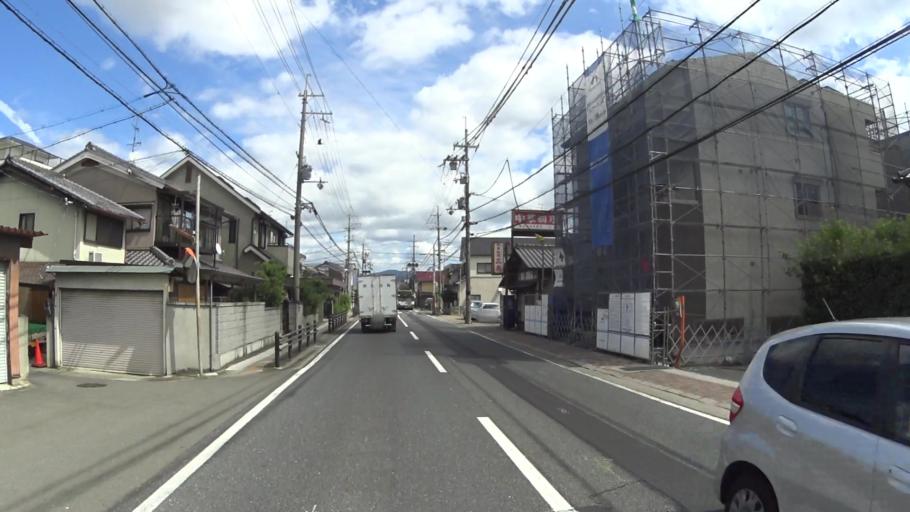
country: JP
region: Kyoto
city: Yawata
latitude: 34.8751
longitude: 135.7498
